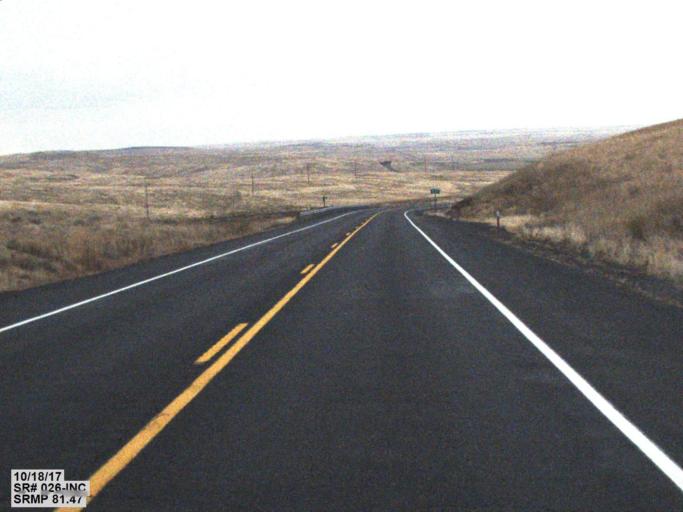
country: US
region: Washington
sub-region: Adams County
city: Ritzville
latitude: 46.7657
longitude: -118.3372
